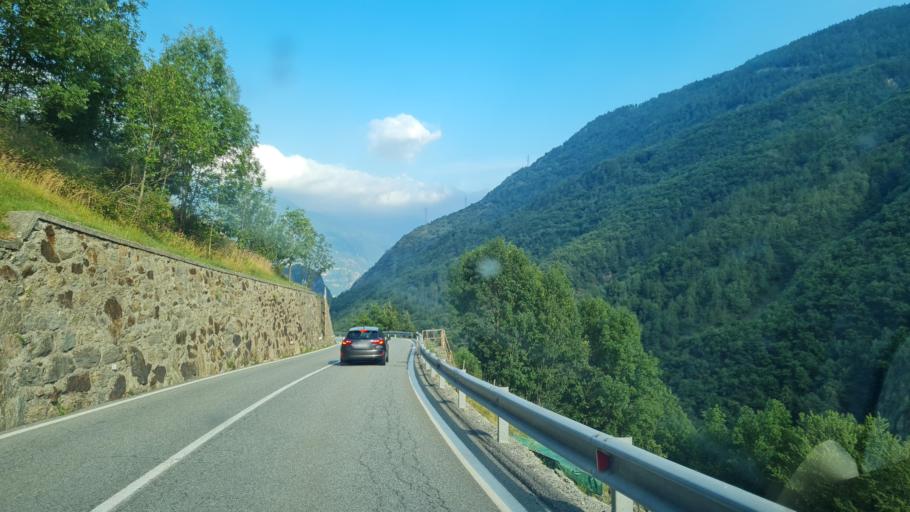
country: IT
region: Aosta Valley
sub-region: Valle d'Aosta
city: Hone
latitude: 45.6114
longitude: 7.7185
